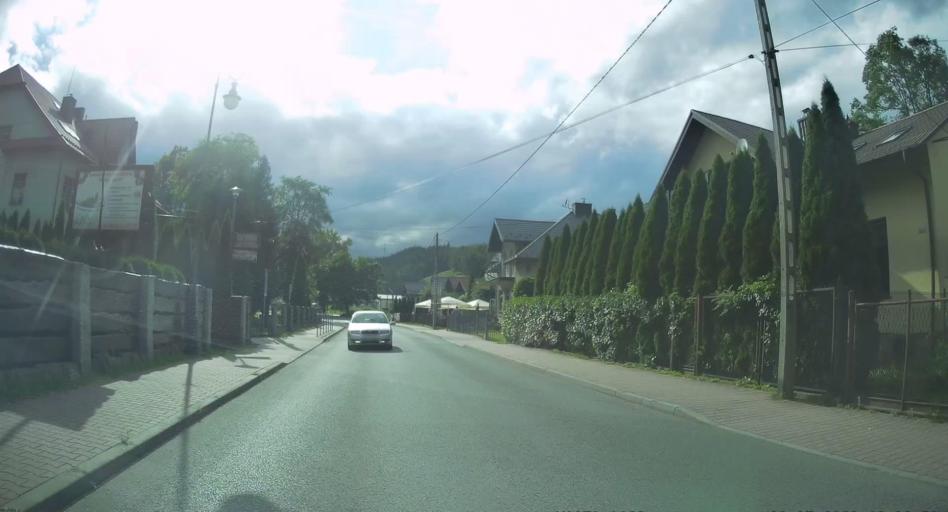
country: PL
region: Lesser Poland Voivodeship
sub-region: Powiat nowosadecki
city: Rytro
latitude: 49.4900
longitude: 20.6772
